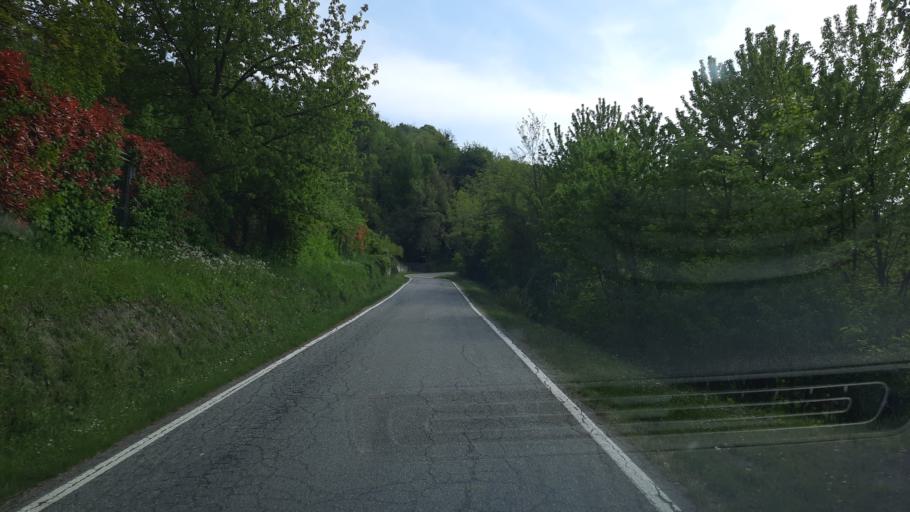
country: IT
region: Piedmont
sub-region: Provincia di Alessandria
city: Camino
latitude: 45.1657
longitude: 8.2631
